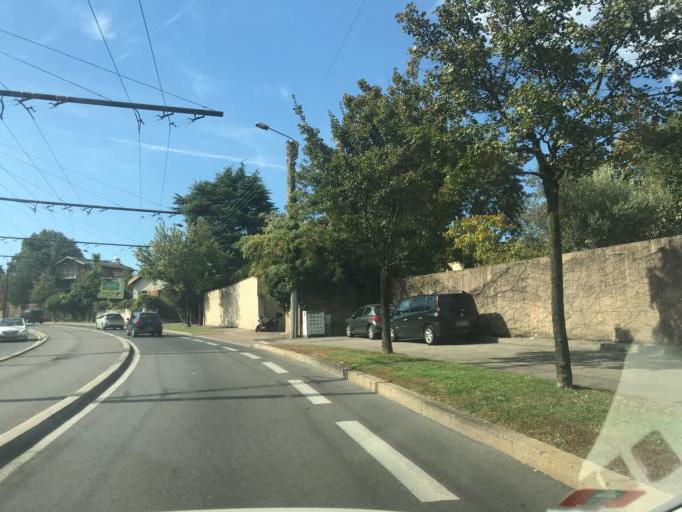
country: FR
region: Rhone-Alpes
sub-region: Departement du Rhone
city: Caluire-et-Cuire
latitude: 45.7974
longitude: 4.8558
